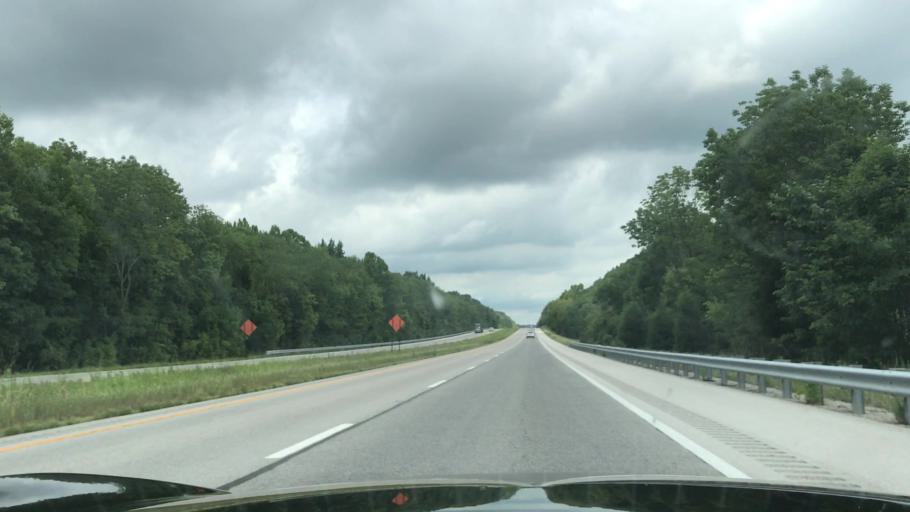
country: US
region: Kentucky
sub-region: Butler County
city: Morgantown
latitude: 37.1405
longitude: -86.6513
